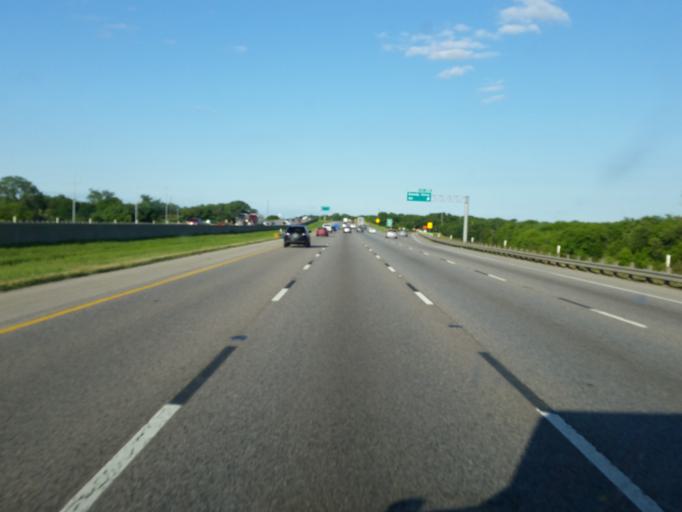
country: US
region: Texas
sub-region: Dallas County
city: Hutchins
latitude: 32.6782
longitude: -96.6818
